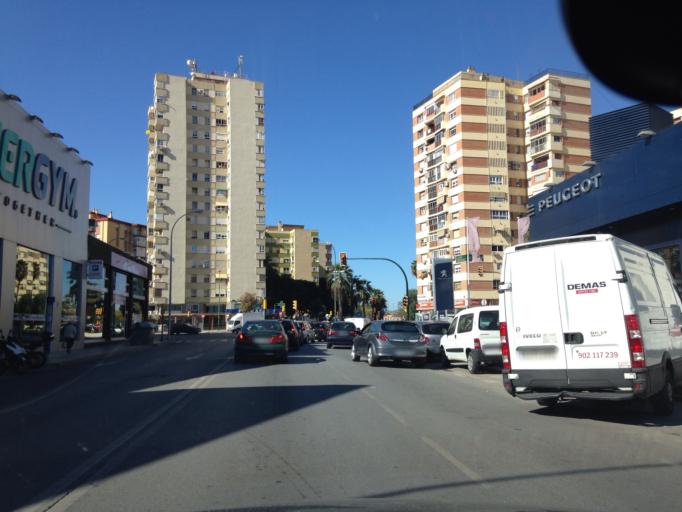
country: ES
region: Andalusia
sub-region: Provincia de Malaga
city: Malaga
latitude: 36.6930
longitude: -4.4532
